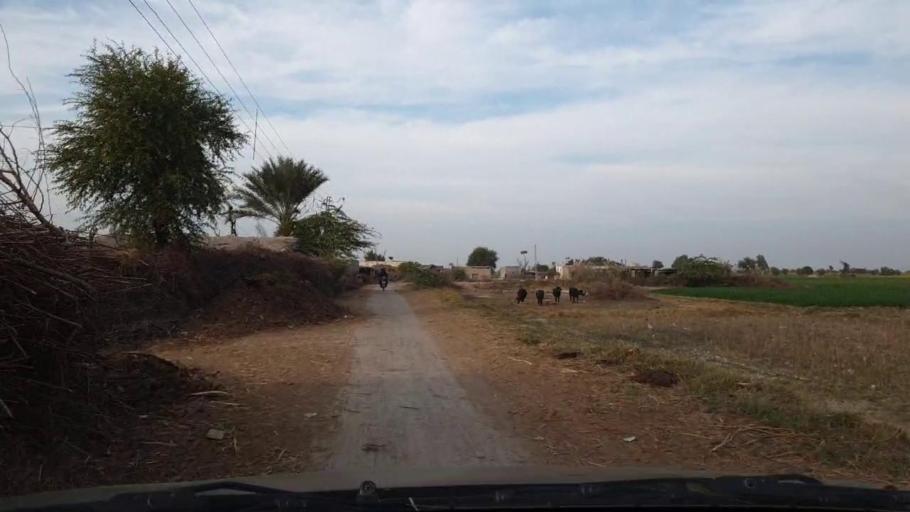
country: PK
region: Sindh
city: Khadro
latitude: 26.1669
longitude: 68.7262
